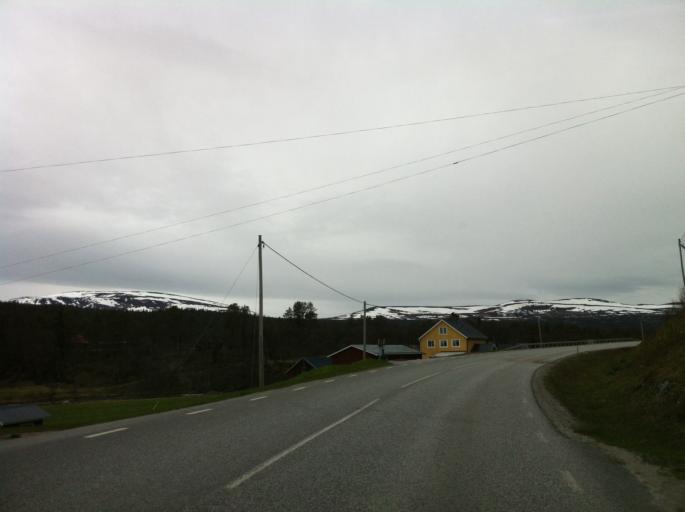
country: NO
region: Sor-Trondelag
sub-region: Tydal
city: Aas
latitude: 62.6186
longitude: 12.4790
